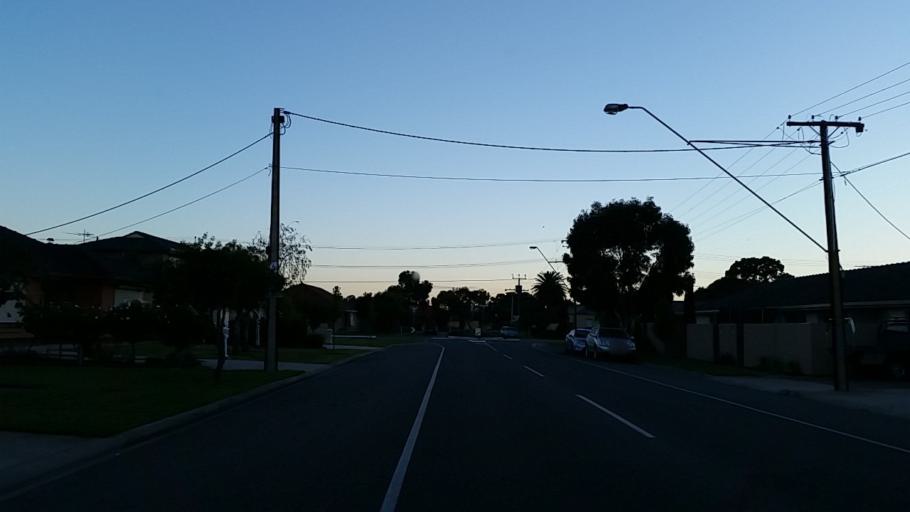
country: AU
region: South Australia
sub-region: Charles Sturt
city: Henley Beach
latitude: -34.9249
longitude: 138.5042
